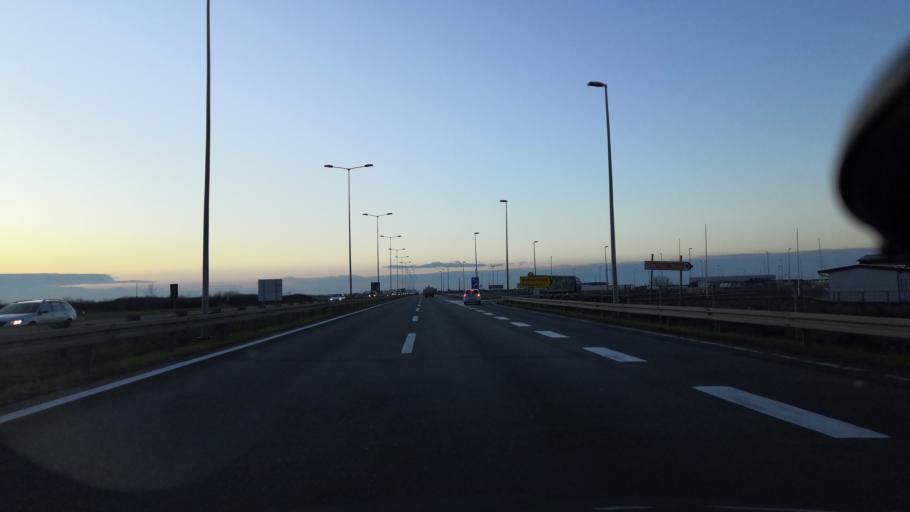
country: RS
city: Dobanovci
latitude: 44.8446
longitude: 20.2096
